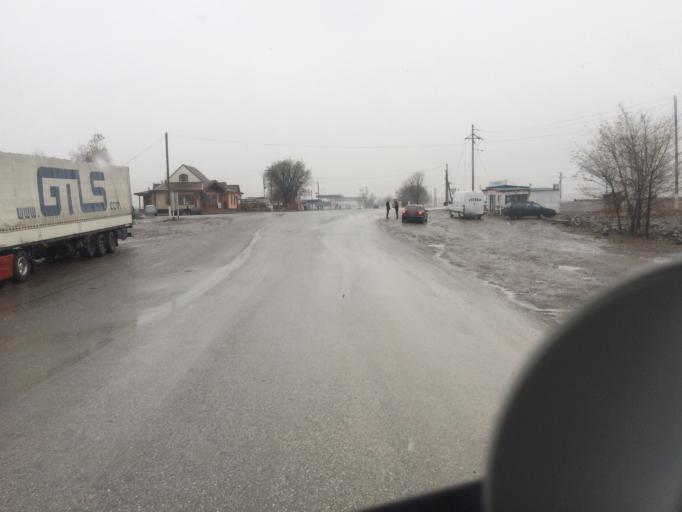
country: KG
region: Chuy
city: Kant
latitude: 43.0006
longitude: 74.8677
